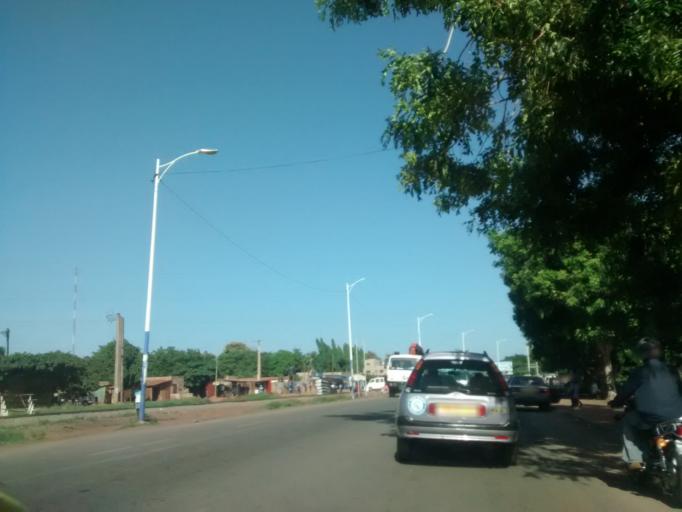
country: TG
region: Maritime
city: Lome
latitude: 6.1690
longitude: 1.1999
